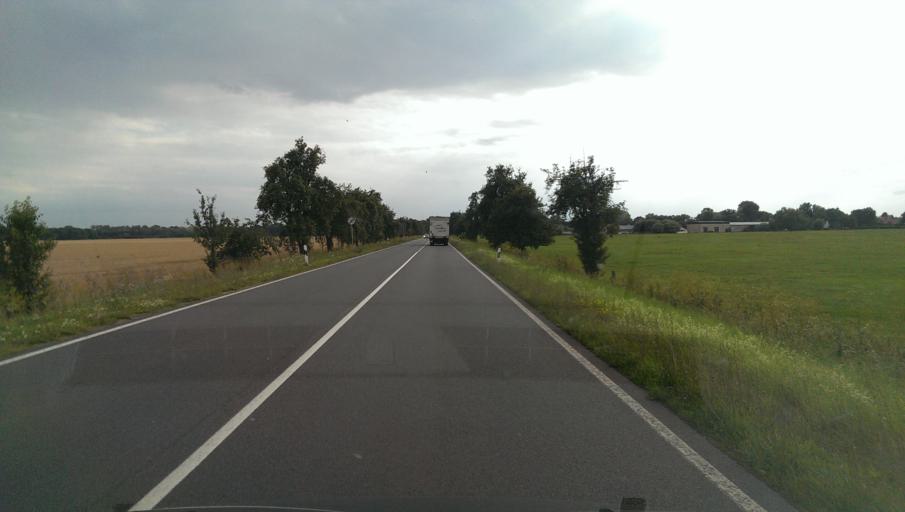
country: DE
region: Saxony
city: Elstertrebnitz
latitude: 51.1451
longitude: 12.2418
